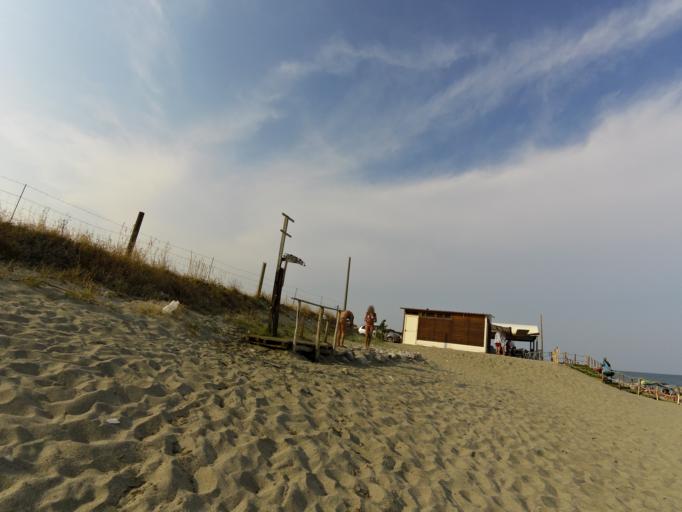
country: IT
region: Calabria
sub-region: Provincia di Reggio Calabria
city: Monasterace Marina
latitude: 38.4183
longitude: 16.5626
